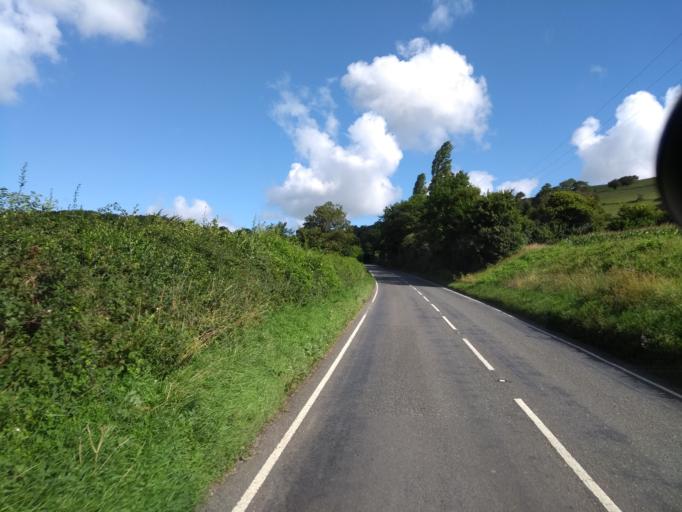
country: GB
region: England
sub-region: Somerset
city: Street
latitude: 51.1025
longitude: -2.7360
